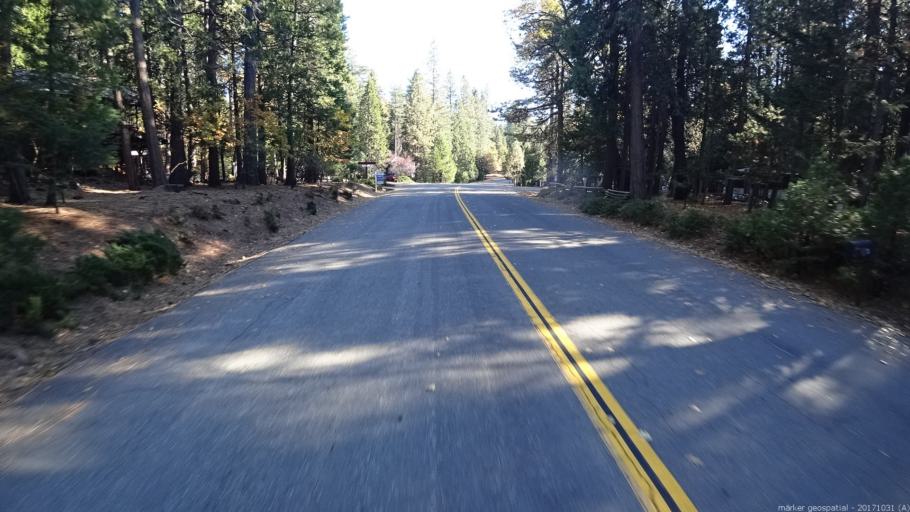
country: US
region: California
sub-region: Shasta County
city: Shingletown
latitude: 40.5020
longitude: -121.9109
